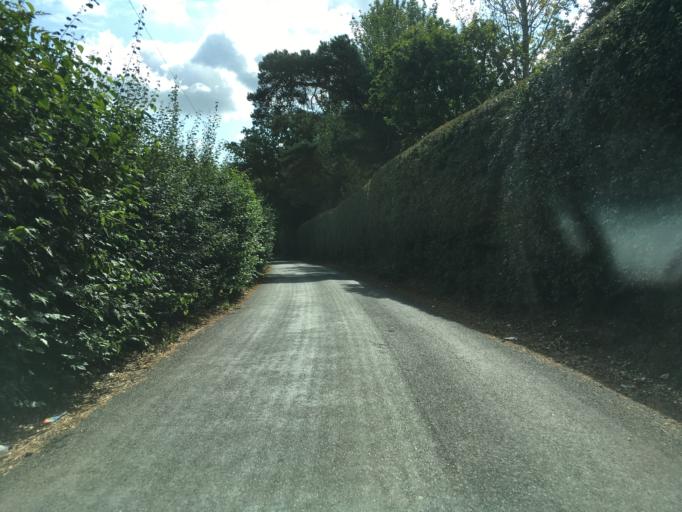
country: GB
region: England
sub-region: Kent
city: Maidstone
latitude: 51.2262
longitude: 0.5487
